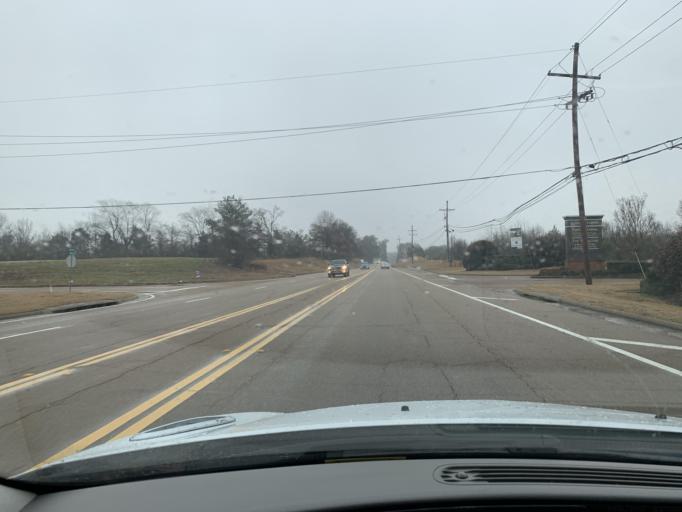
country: US
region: Mississippi
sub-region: De Soto County
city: Horn Lake
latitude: 34.9288
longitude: -90.0115
